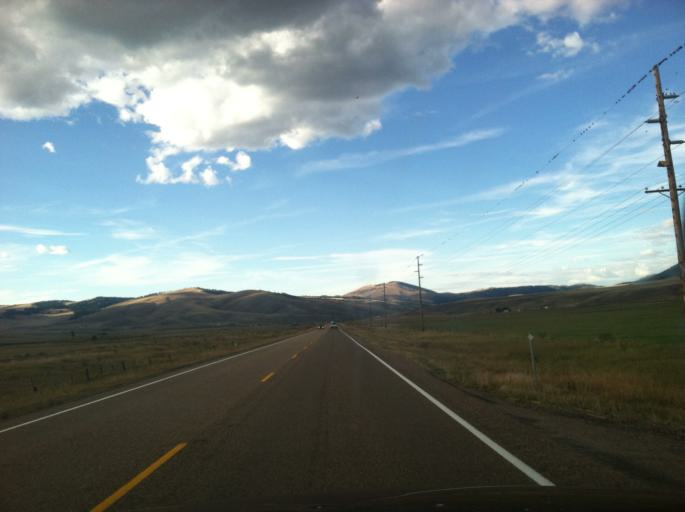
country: US
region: Montana
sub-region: Granite County
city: Philipsburg
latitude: 46.3424
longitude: -113.3121
